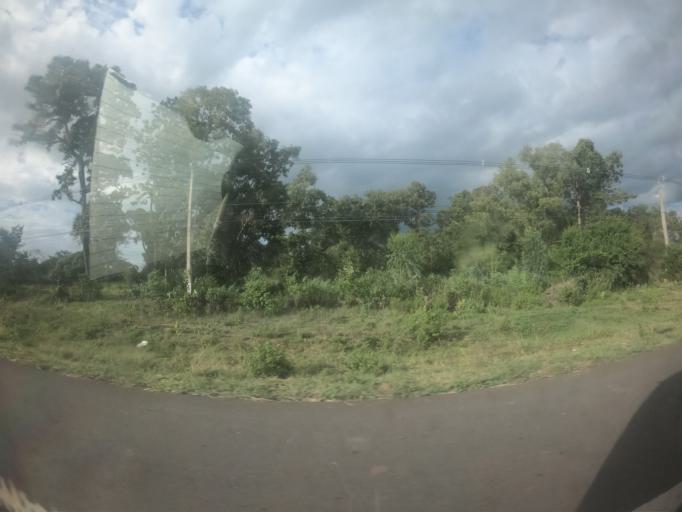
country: TH
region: Surin
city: Kap Choeng
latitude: 14.5250
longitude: 103.5371
